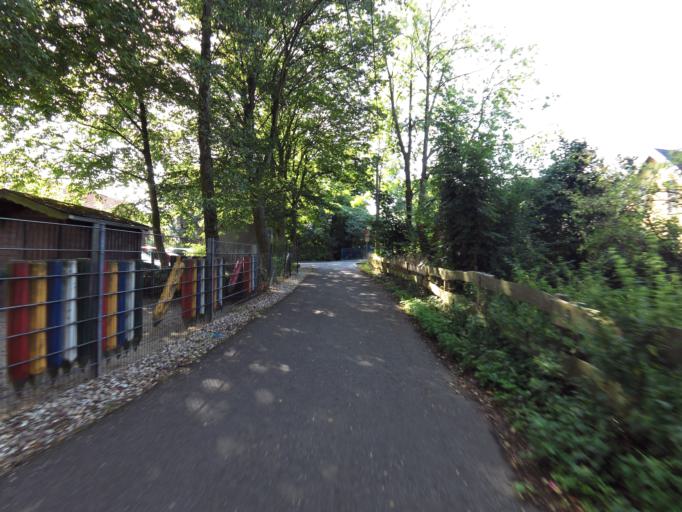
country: DE
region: North Rhine-Westphalia
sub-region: Regierungsbezirk Koln
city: Linnich
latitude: 51.0056
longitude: 6.2420
